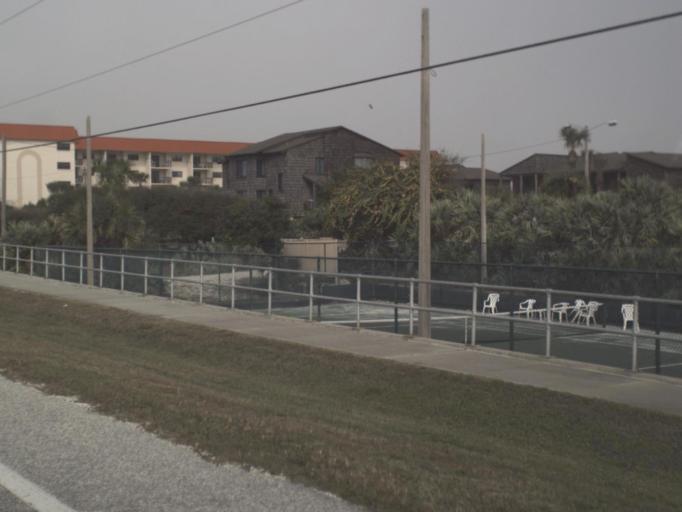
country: US
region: Florida
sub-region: Volusia County
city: Edgewater
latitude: 28.9973
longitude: -80.8719
